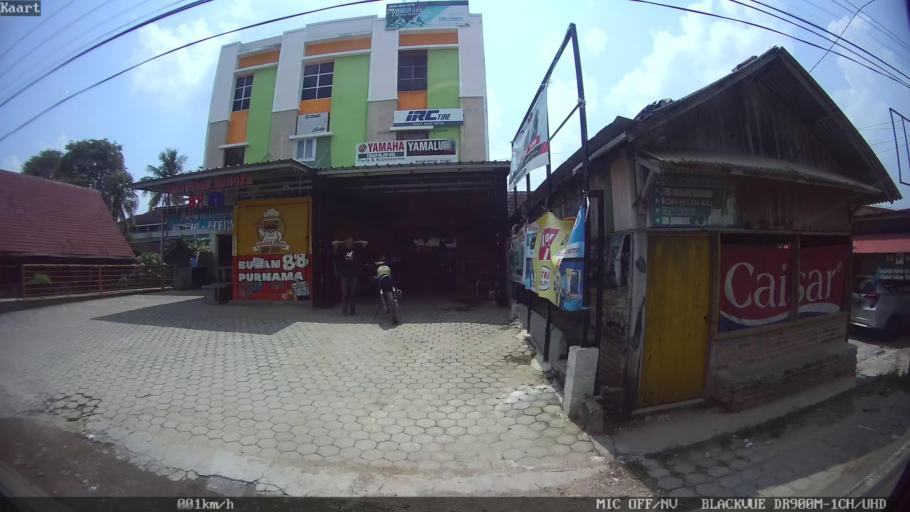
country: ID
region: Lampung
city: Pringsewu
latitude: -5.3596
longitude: 104.9771
